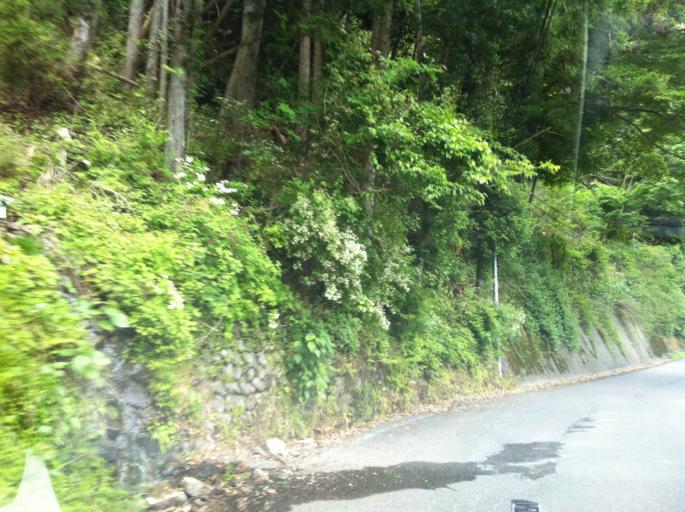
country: JP
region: Shizuoka
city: Shizuoka-shi
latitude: 35.1360
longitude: 138.2932
